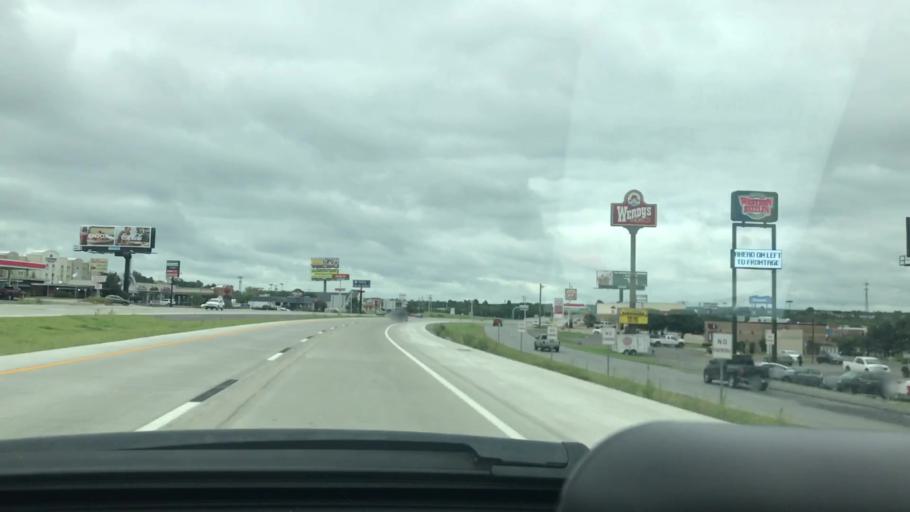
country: US
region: Oklahoma
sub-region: Pittsburg County
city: McAlester
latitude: 34.9174
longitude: -95.7452
